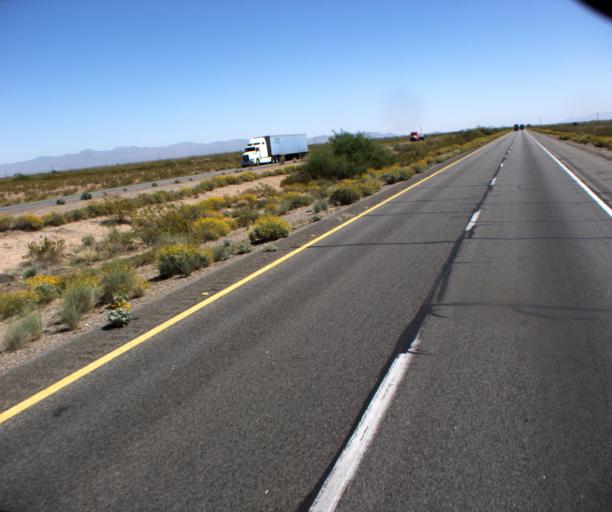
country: US
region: Arizona
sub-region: Maricopa County
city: Buckeye
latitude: 33.4764
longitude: -112.8439
